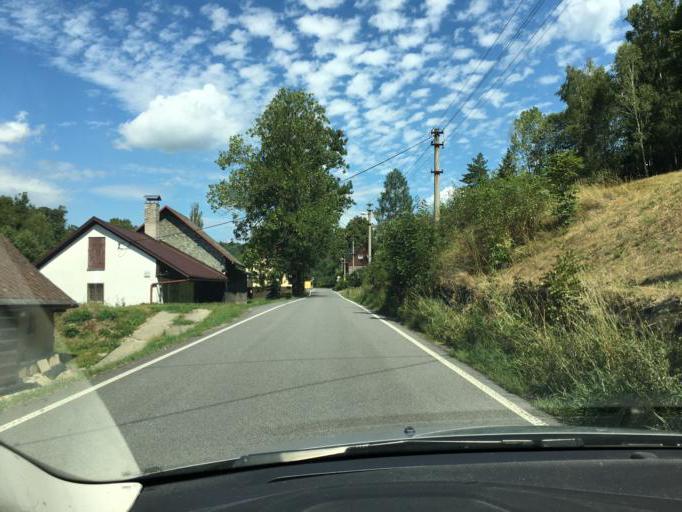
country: CZ
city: Plavy
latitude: 50.7037
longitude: 15.3553
